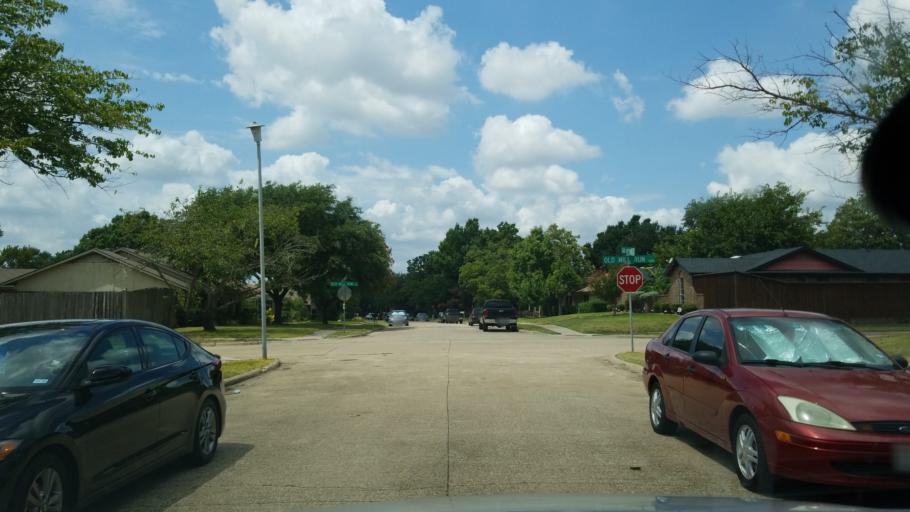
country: US
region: Texas
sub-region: Dallas County
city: Garland
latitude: 32.9279
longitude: -96.6520
